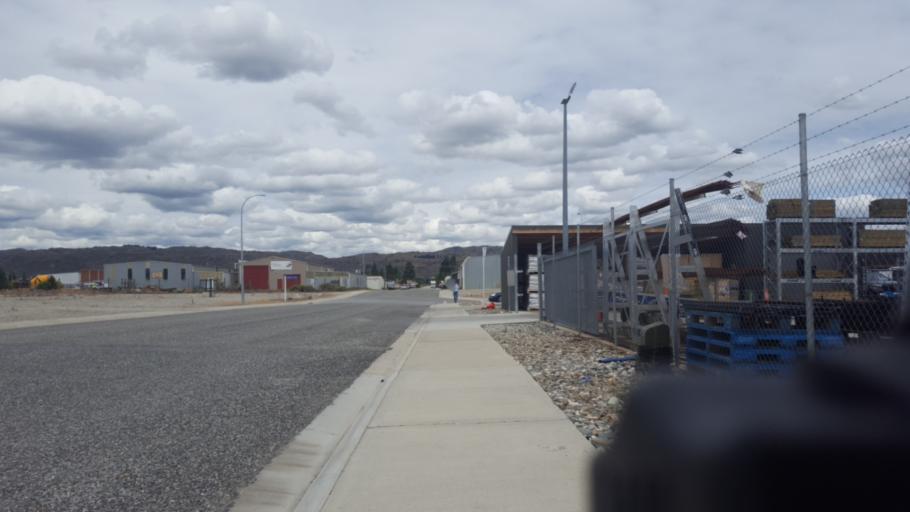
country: NZ
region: Otago
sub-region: Queenstown-Lakes District
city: Wanaka
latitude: -45.2466
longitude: 169.3716
